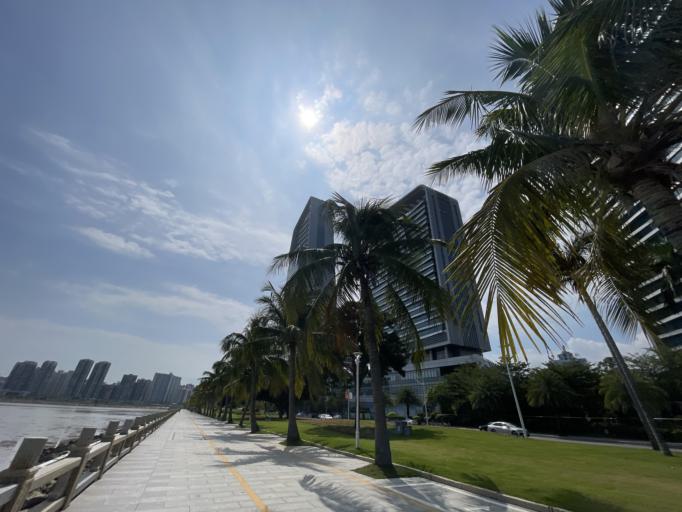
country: MO
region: Macau
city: Macau
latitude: 22.2235
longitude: 113.5554
